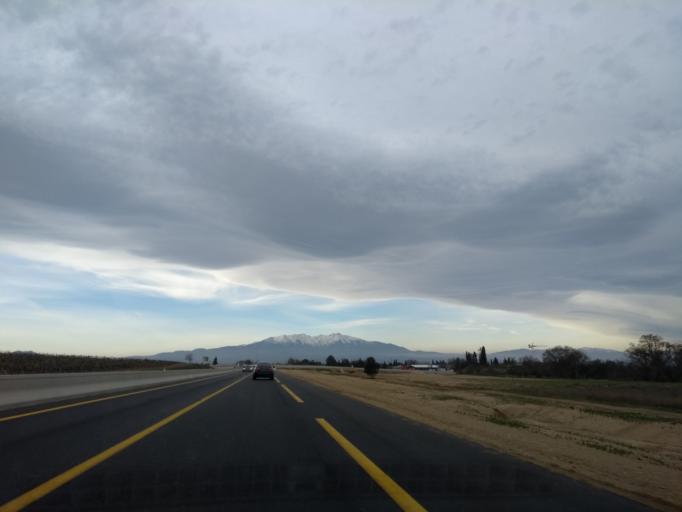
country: FR
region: Languedoc-Roussillon
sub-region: Departement des Pyrenees-Orientales
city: Perpignan
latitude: 42.6767
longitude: 2.8681
